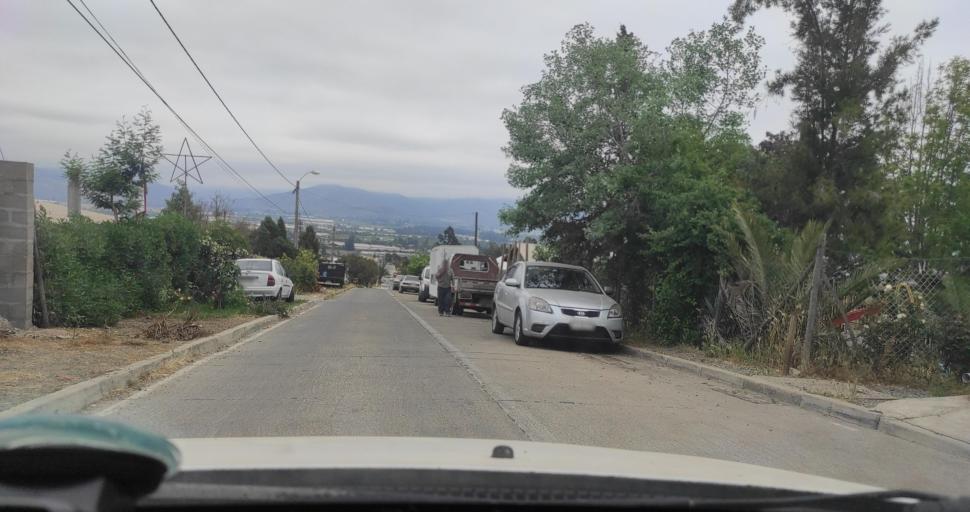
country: CL
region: Valparaiso
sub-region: Provincia de Marga Marga
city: Limache
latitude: -32.9852
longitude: -71.2245
